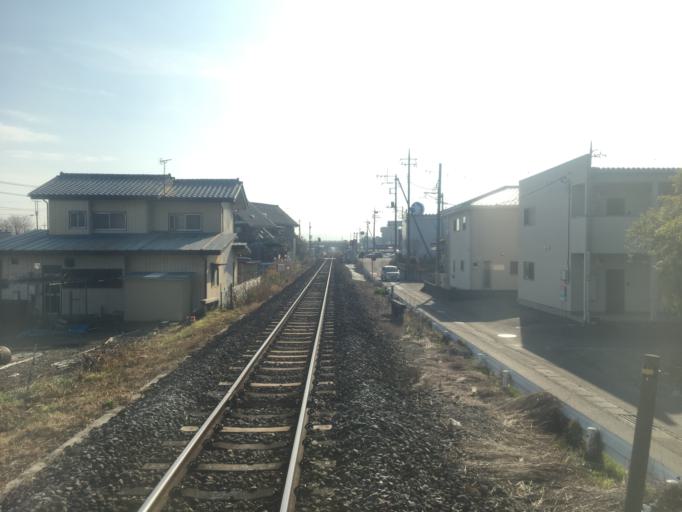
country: JP
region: Gunma
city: Fujioka
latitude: 36.2545
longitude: 139.0834
